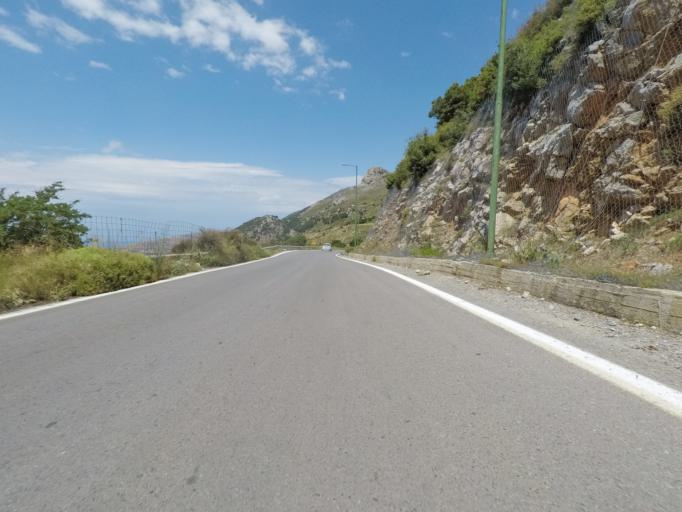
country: GR
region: Crete
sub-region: Nomos Irakleiou
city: Mokhos
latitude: 35.2078
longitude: 25.4585
